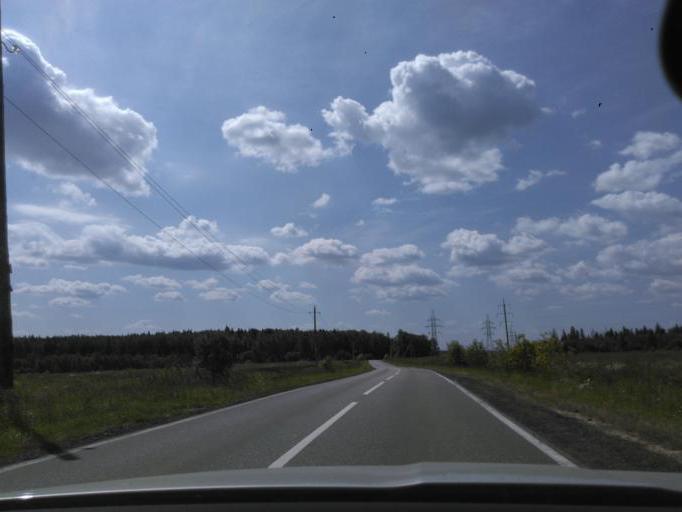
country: RU
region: Moskovskaya
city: Solnechnogorsk
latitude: 56.1451
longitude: 36.9786
